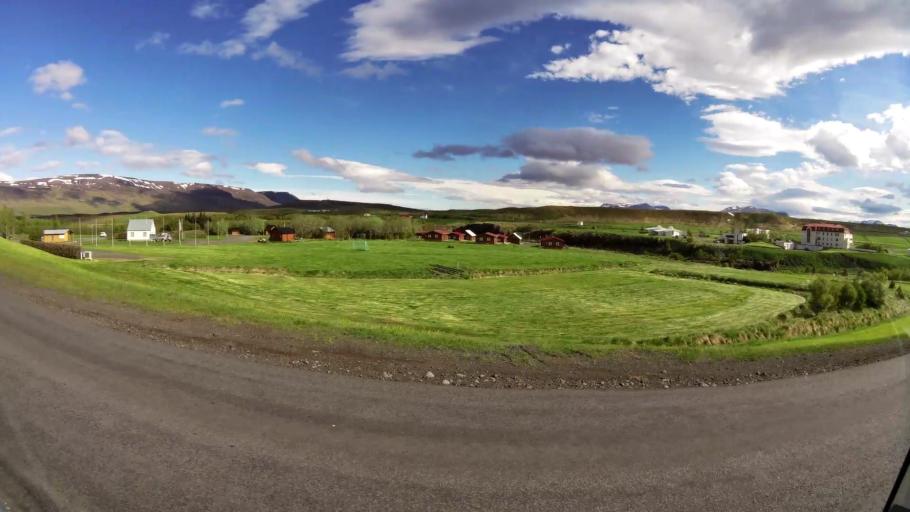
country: IS
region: Northwest
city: Saudarkrokur
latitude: 65.6593
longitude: -20.2793
